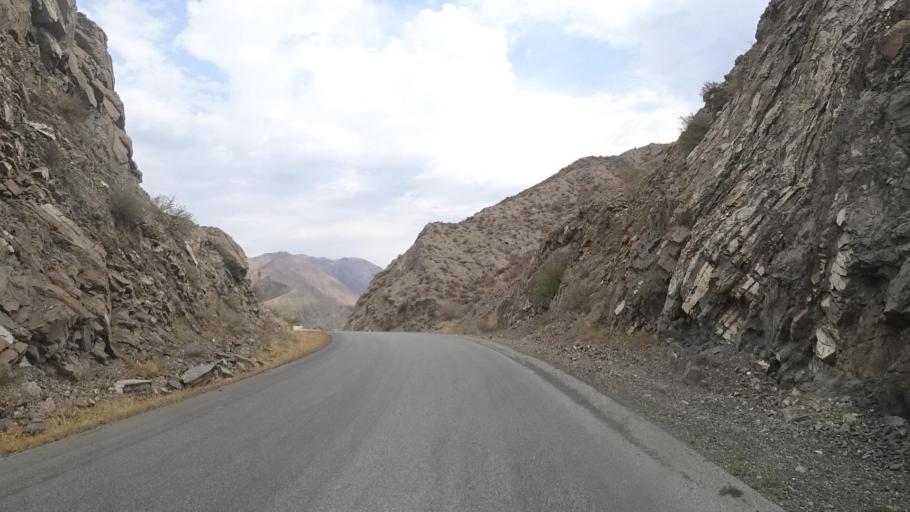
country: KG
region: Jalal-Abad
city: Tash-Kumyr
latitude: 41.5031
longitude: 72.3907
